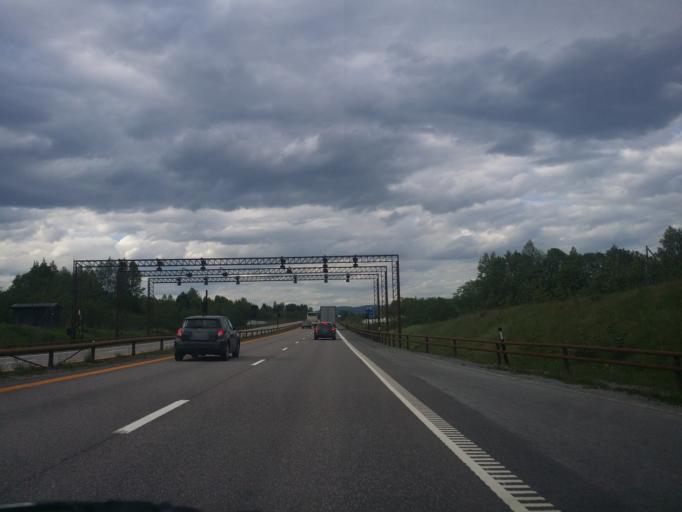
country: NO
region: Akershus
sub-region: Eidsvoll
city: Eidsvoll
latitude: 60.3710
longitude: 11.2054
